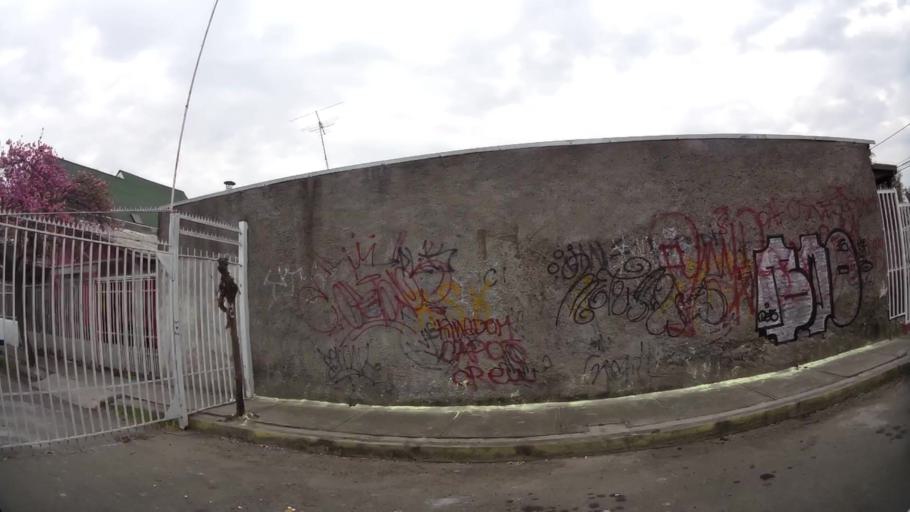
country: CL
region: Santiago Metropolitan
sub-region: Provincia de Santiago
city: Lo Prado
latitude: -33.4947
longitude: -70.7366
